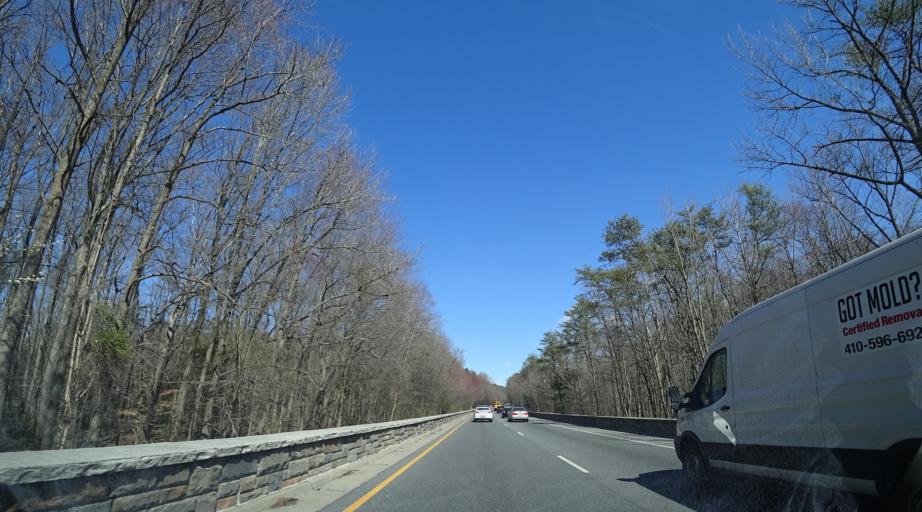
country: US
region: Maryland
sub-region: Prince George's County
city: New Carrollton
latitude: 38.9826
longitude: -76.8925
